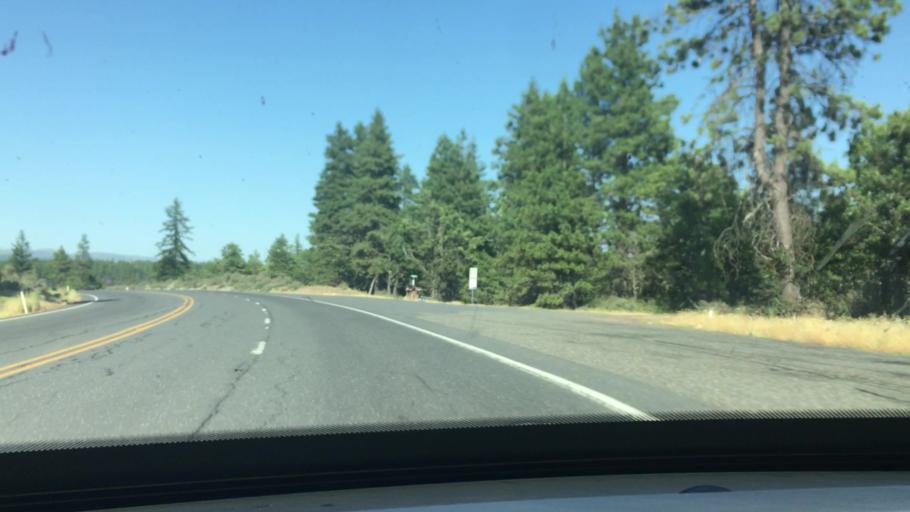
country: US
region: Washington
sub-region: Klickitat County
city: Goldendale
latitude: 45.8981
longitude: -120.7143
